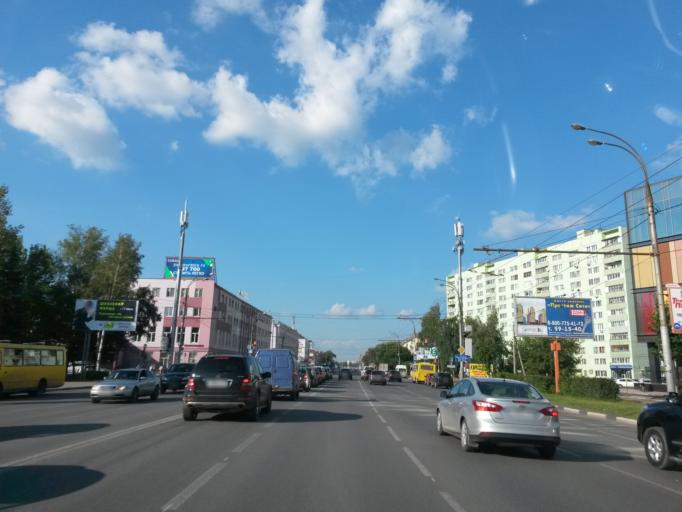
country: RU
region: Ivanovo
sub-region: Gorod Ivanovo
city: Ivanovo
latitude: 56.9751
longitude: 40.9748
